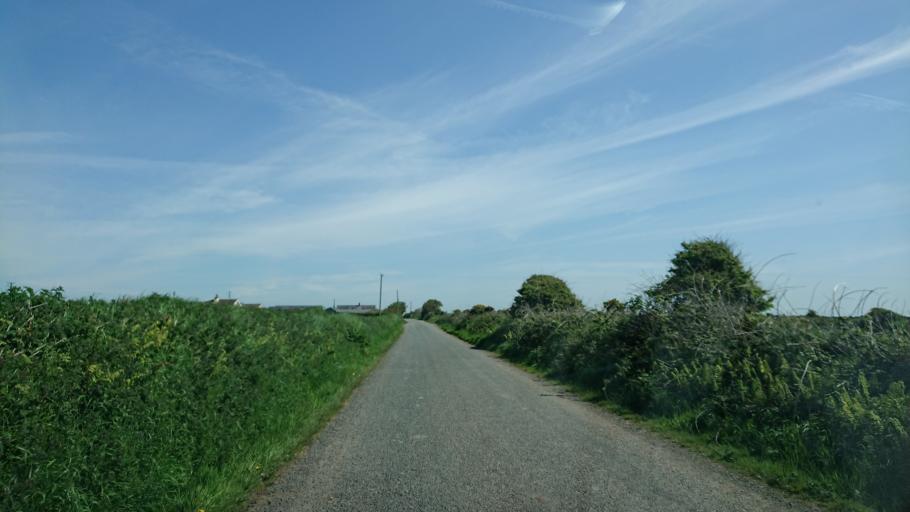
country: IE
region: Munster
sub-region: Waterford
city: Tra Mhor
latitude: 52.1439
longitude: -7.0841
